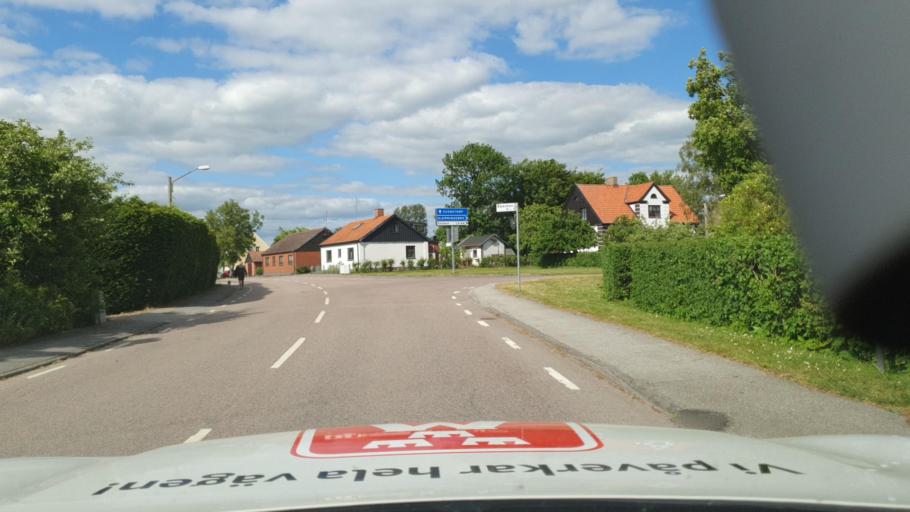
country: SE
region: Skane
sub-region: Ystads Kommun
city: Kopingebro
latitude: 55.4712
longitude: 13.9465
